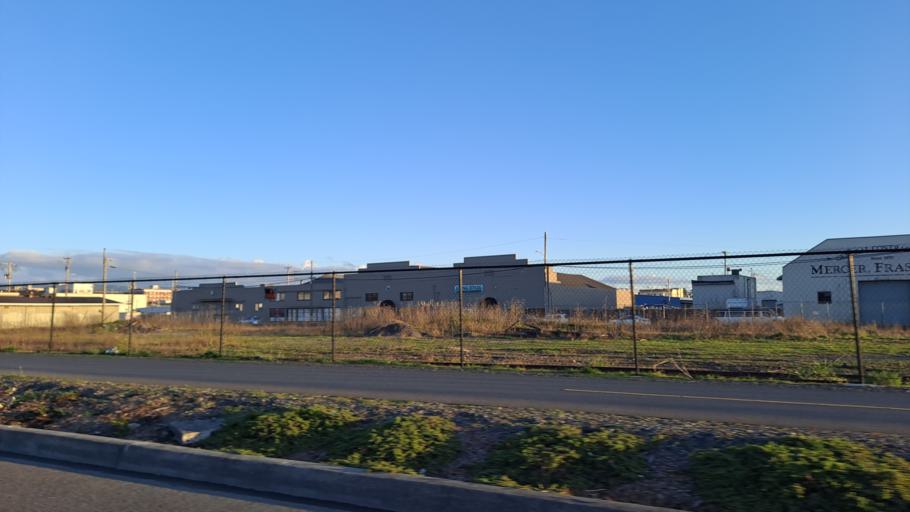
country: US
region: California
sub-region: Humboldt County
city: Eureka
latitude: 40.8041
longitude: -124.1736
